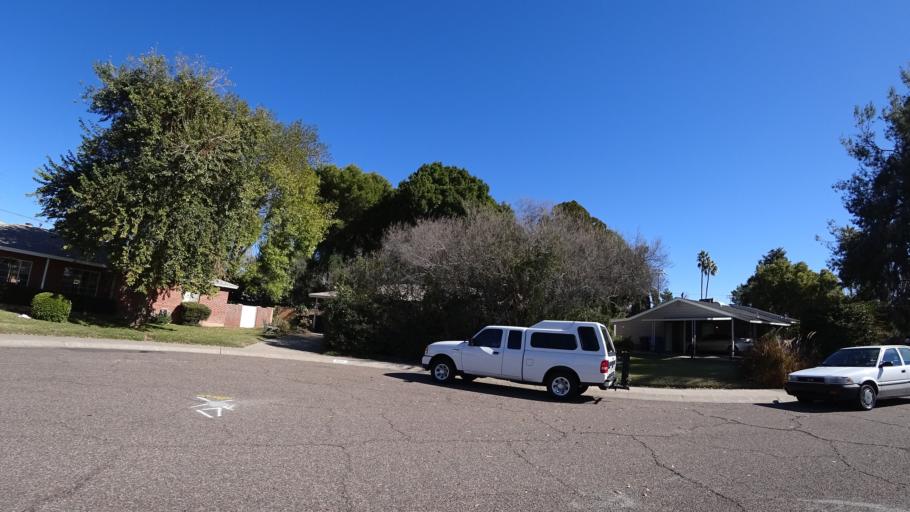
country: US
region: Arizona
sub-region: Maricopa County
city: Phoenix
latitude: 33.5266
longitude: -112.0595
